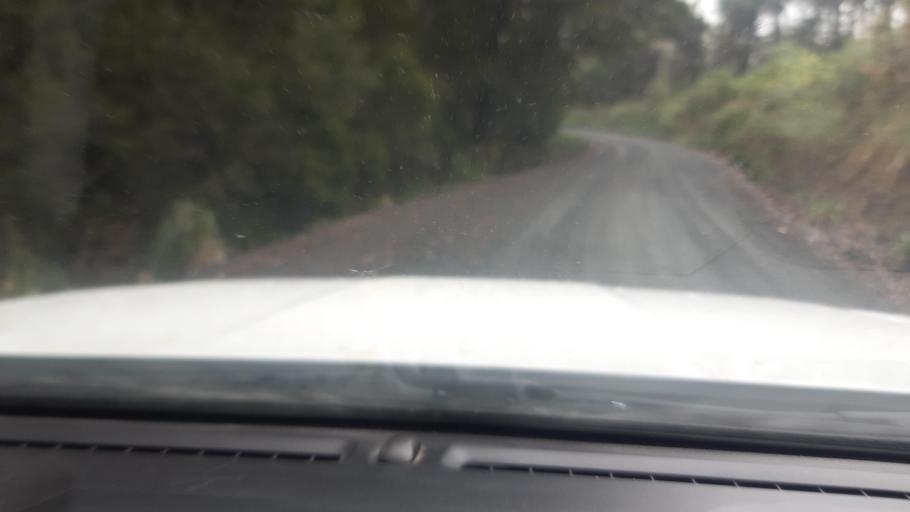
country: NZ
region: Northland
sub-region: Far North District
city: Kaitaia
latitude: -34.9841
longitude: 173.2058
